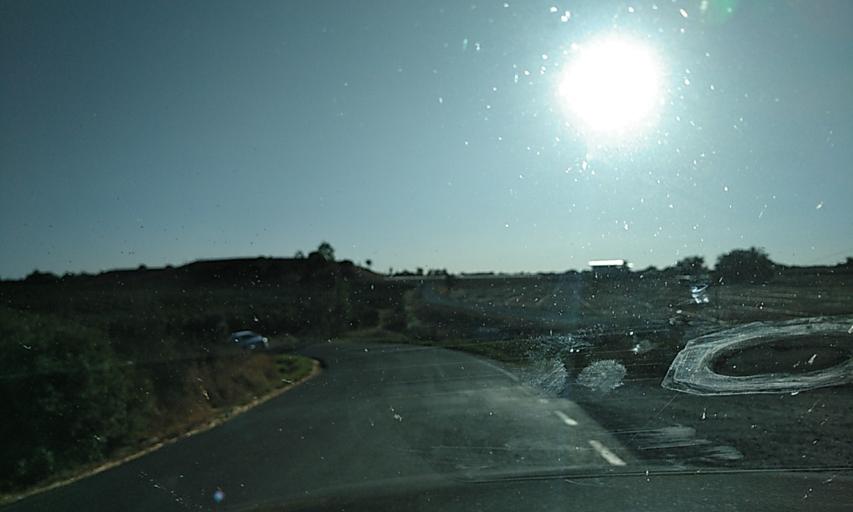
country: ES
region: Andalusia
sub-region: Provincia de Huelva
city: San Bartolome de la Torre
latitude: 37.4140
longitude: -7.1190
